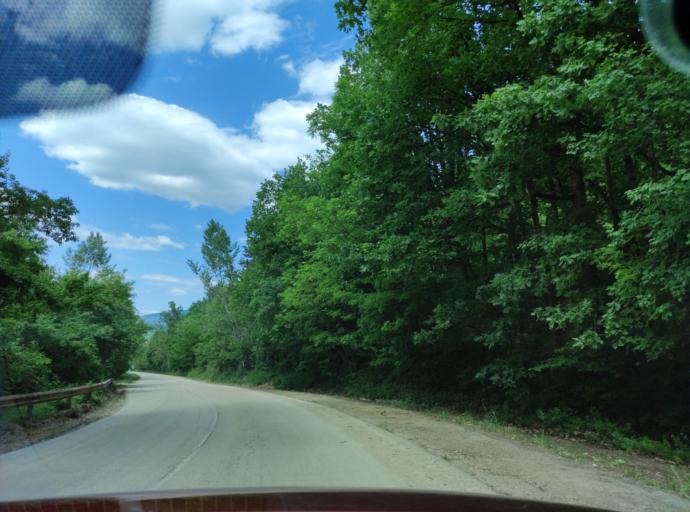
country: BG
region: Montana
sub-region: Obshtina Montana
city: Montana
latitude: 43.3868
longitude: 23.0769
